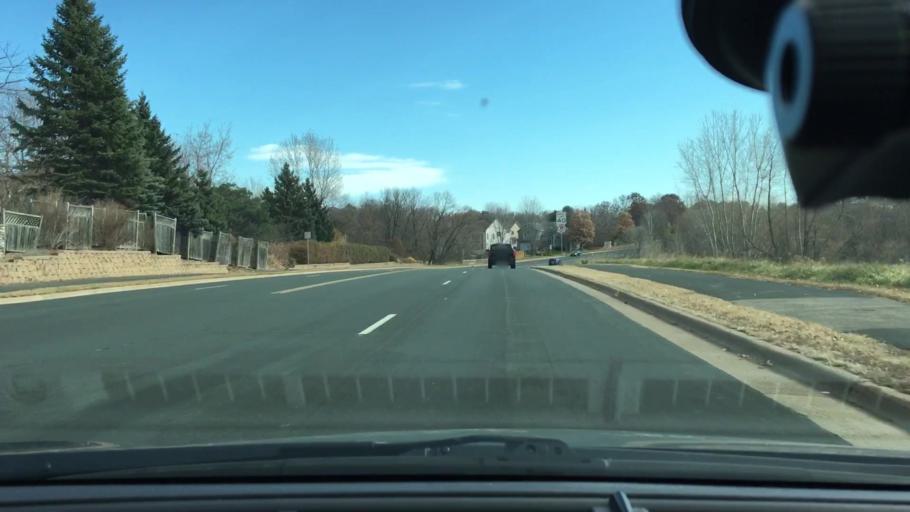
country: US
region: Minnesota
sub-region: Hennepin County
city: Maple Grove
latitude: 45.1070
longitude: -93.4809
